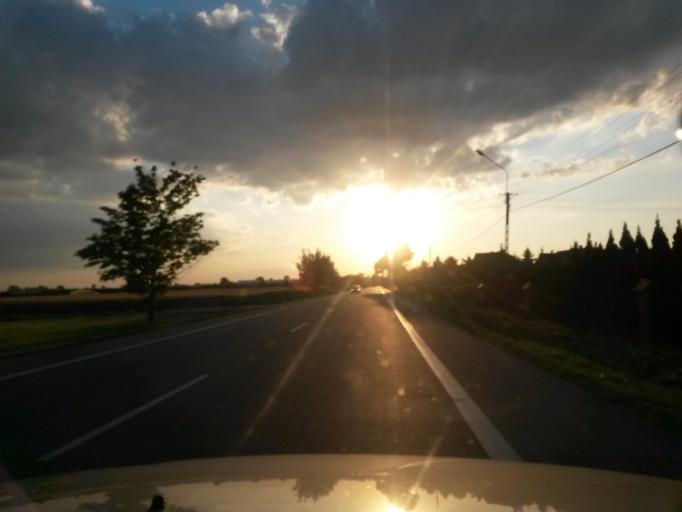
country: PL
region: Lodz Voivodeship
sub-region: Powiat wielunski
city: Czarnozyly
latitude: 51.2574
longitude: 18.4912
